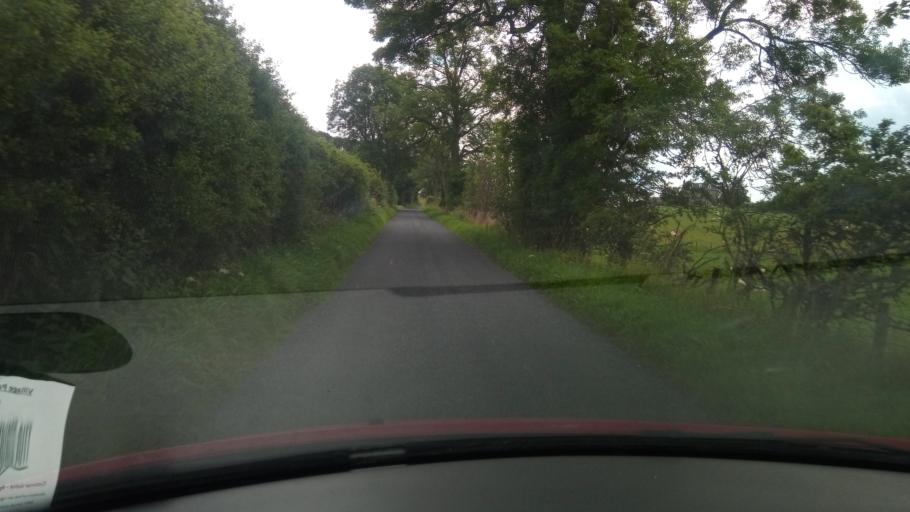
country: GB
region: Scotland
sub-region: The Scottish Borders
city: Jedburgh
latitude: 55.4026
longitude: -2.6492
